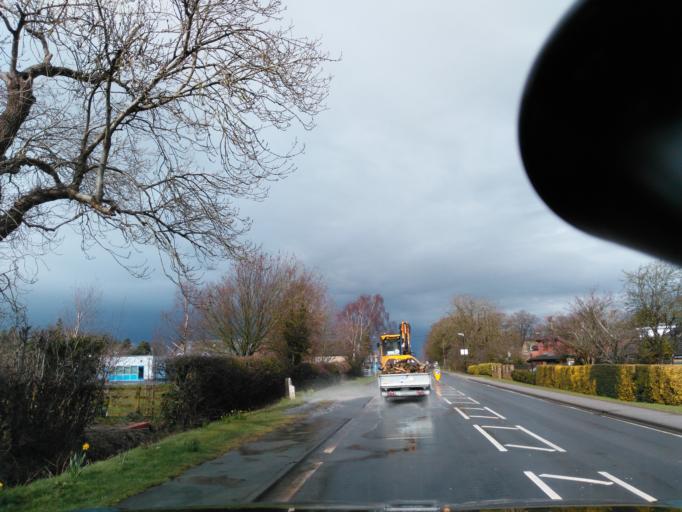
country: GB
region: England
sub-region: North Yorkshire
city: Harrogate
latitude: 54.0189
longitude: -1.5691
